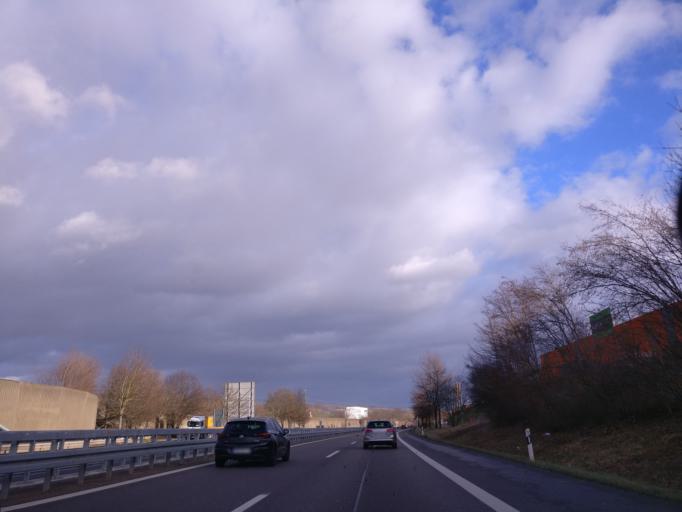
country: DE
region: Baden-Wuerttemberg
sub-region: Regierungsbezirk Stuttgart
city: Weinstadt-Endersbach
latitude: 48.8150
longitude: 9.3597
